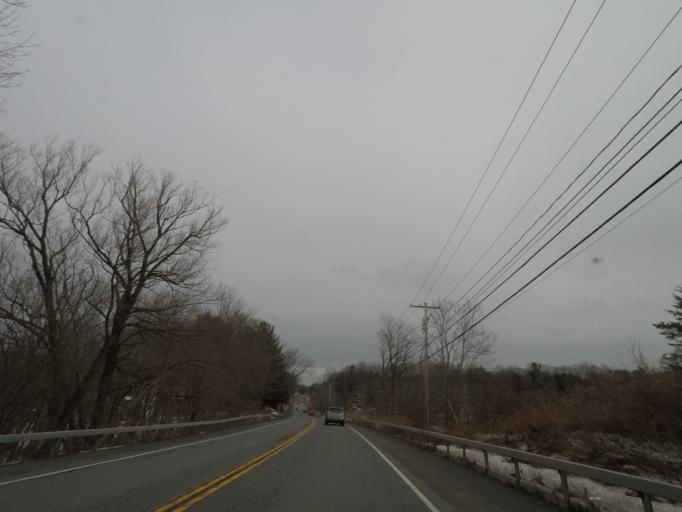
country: US
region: New York
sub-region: Albany County
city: Voorheesville
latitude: 42.7023
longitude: -73.9410
